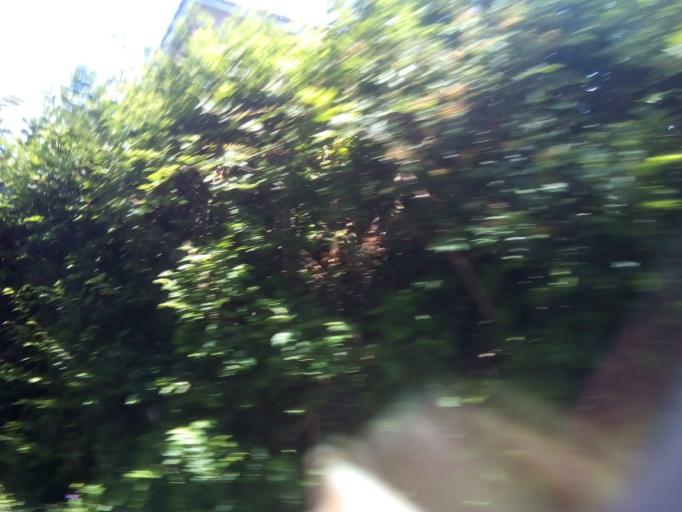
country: IE
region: Leinster
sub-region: Loch Garman
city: Loch Garman
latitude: 52.2349
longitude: -6.5955
